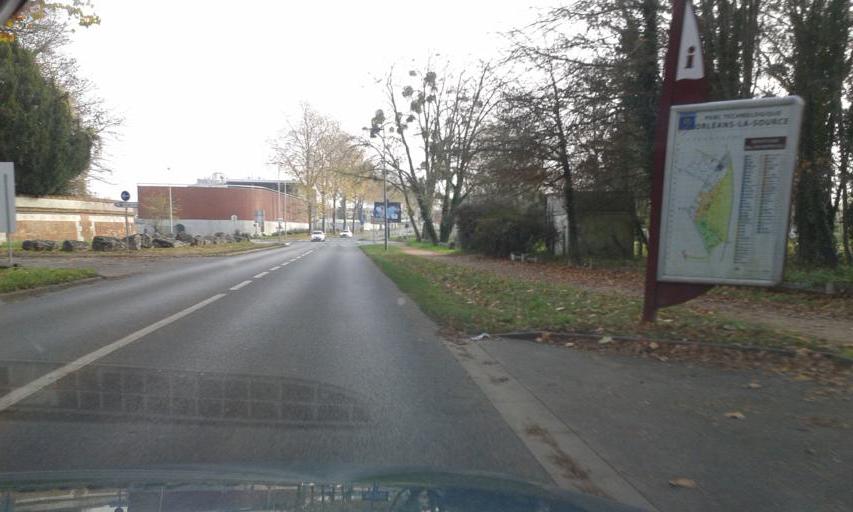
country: FR
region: Centre
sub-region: Departement du Loiret
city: Saint-Cyr-en-Val
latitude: 47.8467
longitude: 1.9395
